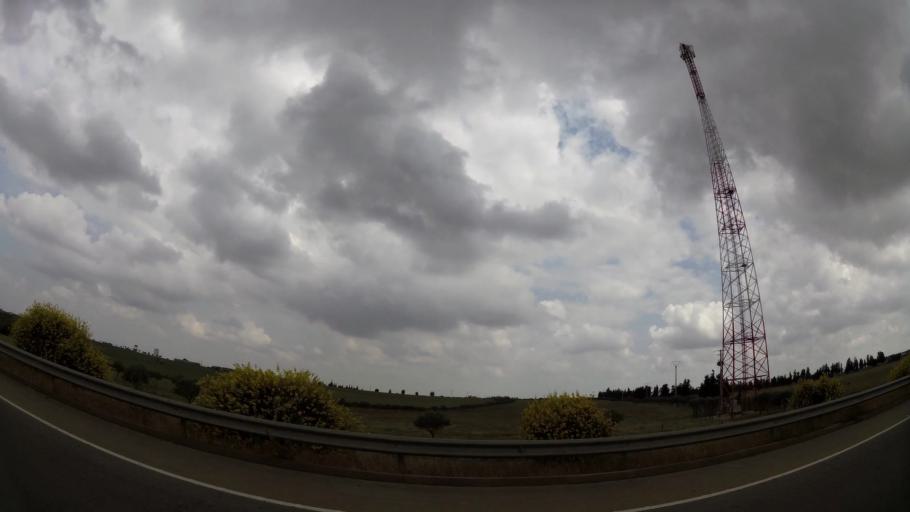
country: MA
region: Rabat-Sale-Zemmour-Zaer
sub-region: Khemisset
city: Tiflet
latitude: 33.8924
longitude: -6.3605
